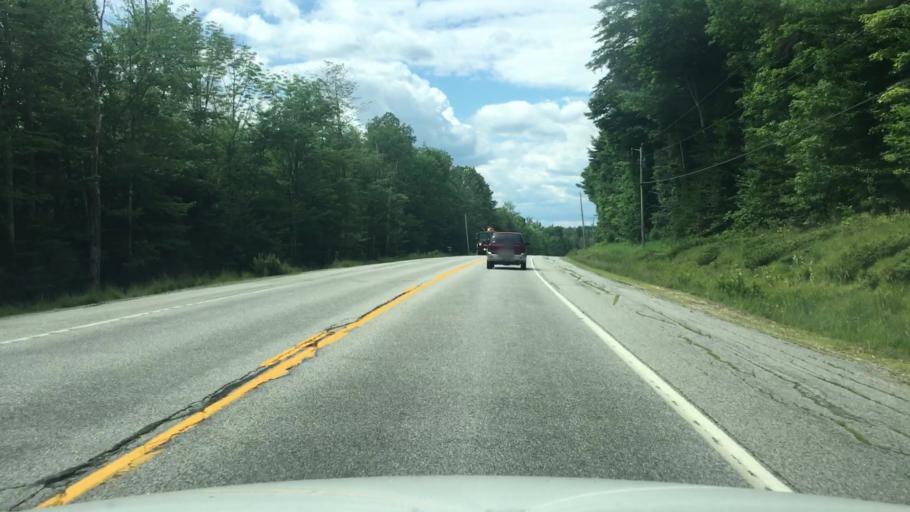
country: US
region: Maine
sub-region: Oxford County
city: West Paris
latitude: 44.3683
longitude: -70.5982
